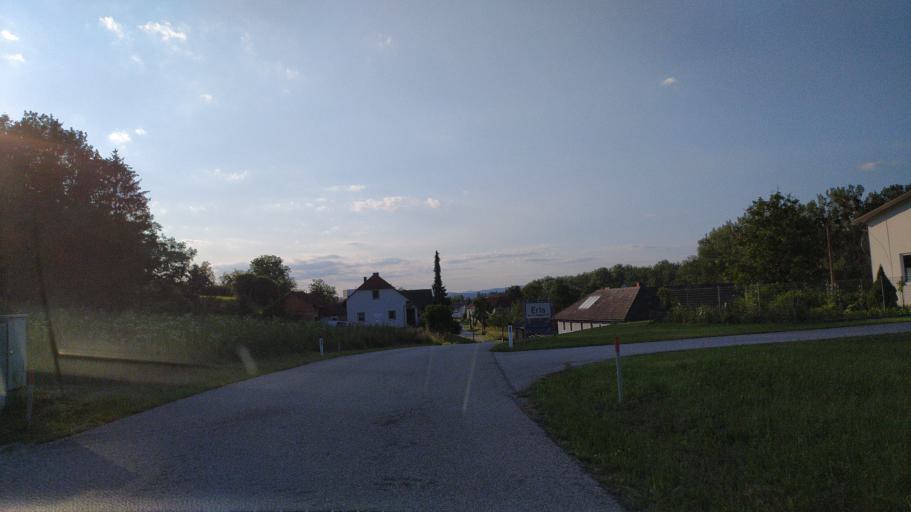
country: AT
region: Lower Austria
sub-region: Politischer Bezirk Amstetten
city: Sankt Valentin
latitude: 48.1993
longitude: 14.5770
